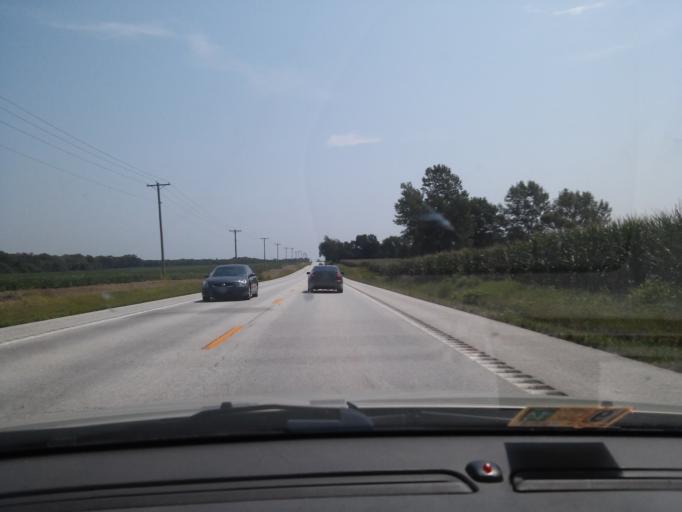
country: US
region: Missouri
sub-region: Pike County
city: Bowling Green
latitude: 39.3445
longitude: -91.2882
